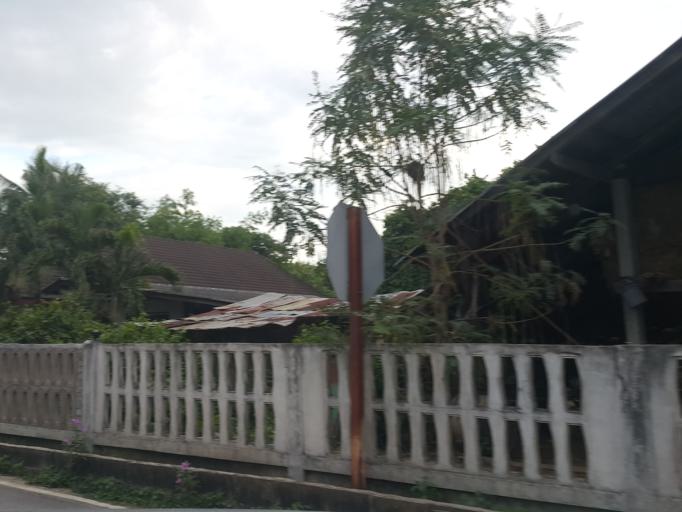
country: TH
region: Chiang Mai
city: San Sai
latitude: 18.8791
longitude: 99.0891
